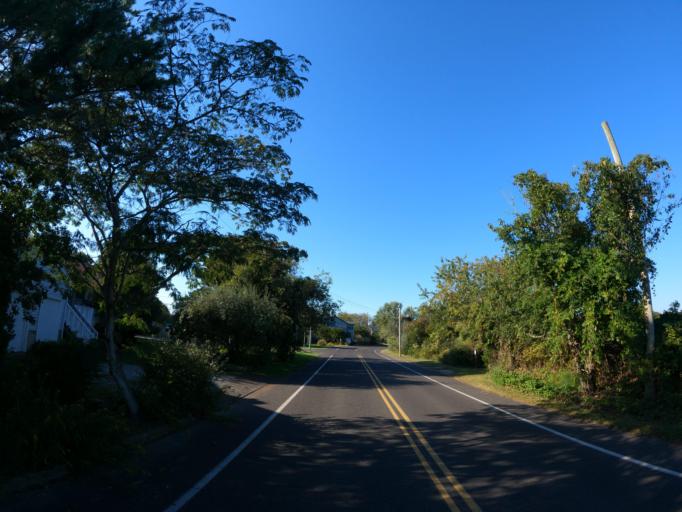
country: US
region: New Jersey
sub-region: Cape May County
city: West Cape May
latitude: 38.9339
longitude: -74.9617
